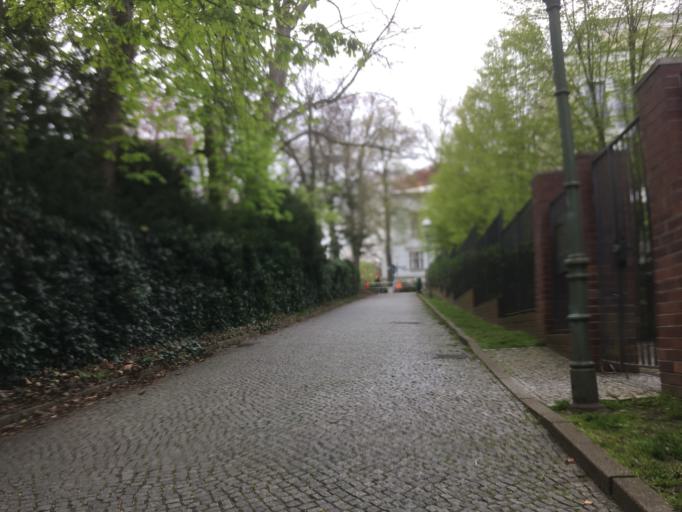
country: DE
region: Berlin
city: Grunewald
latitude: 52.4883
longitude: 13.2702
